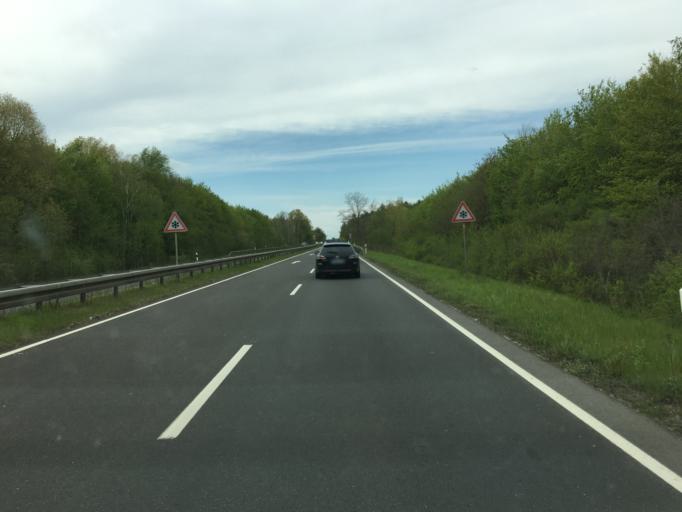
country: DE
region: North Rhine-Westphalia
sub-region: Regierungsbezirk Koln
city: Erftstadt
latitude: 50.8247
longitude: 6.8305
